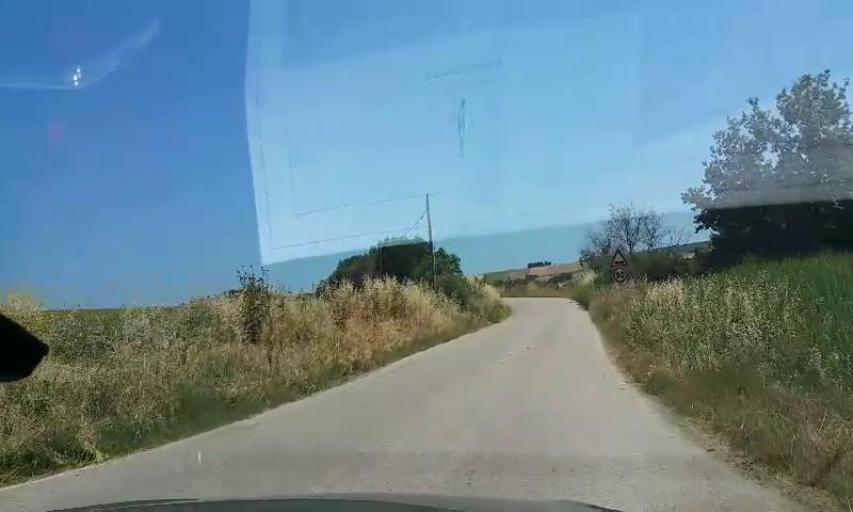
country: IT
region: Molise
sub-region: Provincia di Campobasso
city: Guglionesi
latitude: 41.9425
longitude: 14.8973
